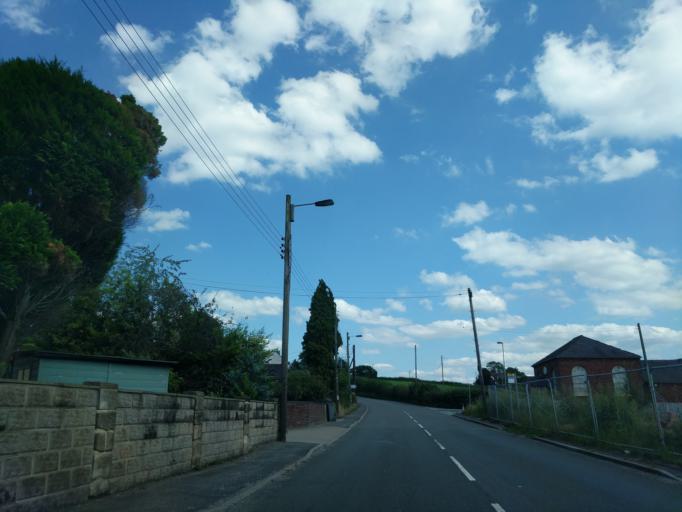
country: GB
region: England
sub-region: Staffordshire
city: Cheadle
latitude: 52.9338
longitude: -1.9361
